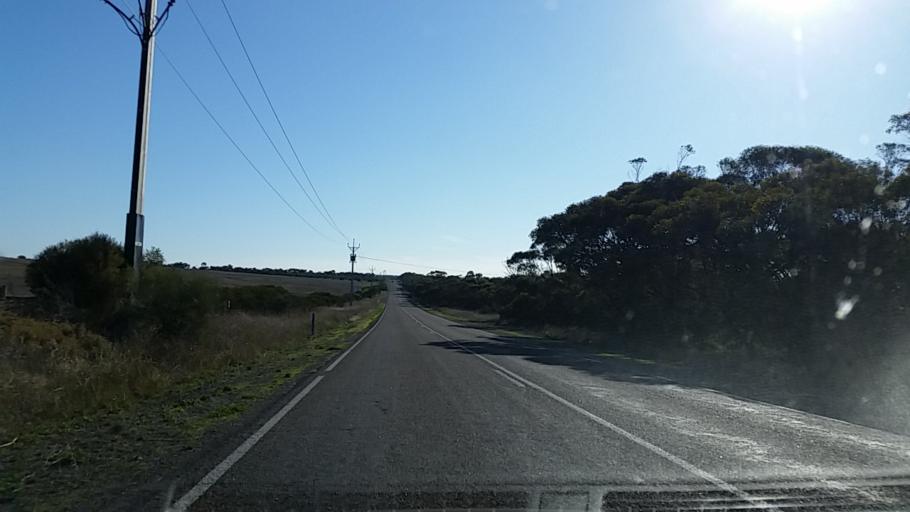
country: AU
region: South Australia
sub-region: Murray Bridge
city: Murray Bridge
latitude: -35.1220
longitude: 139.1743
